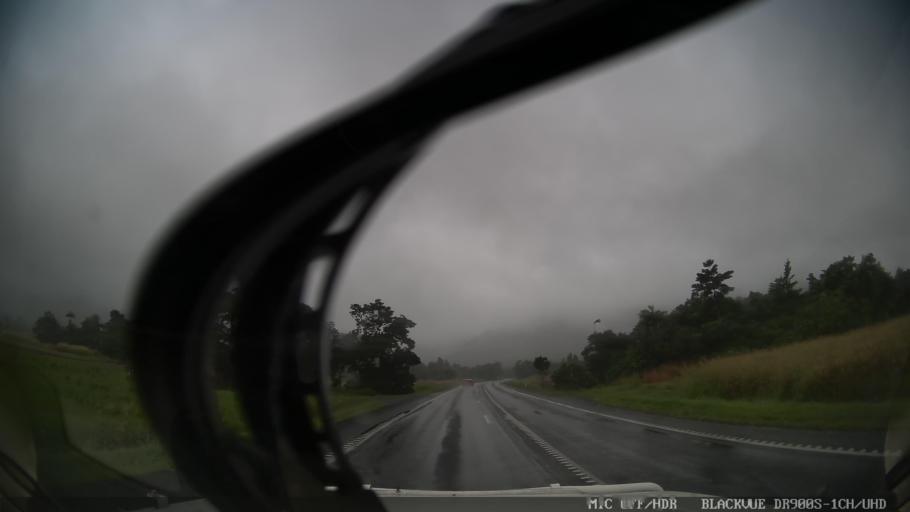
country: AU
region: Queensland
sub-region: Cassowary Coast
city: Innisfail
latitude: -17.8665
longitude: 145.9810
